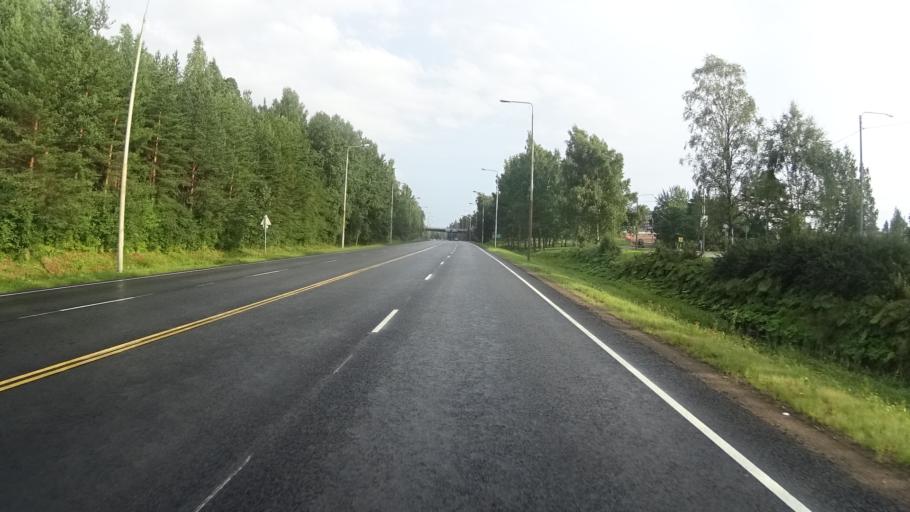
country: FI
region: Kymenlaakso
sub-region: Kotka-Hamina
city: Kotka
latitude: 60.4830
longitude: 26.9109
